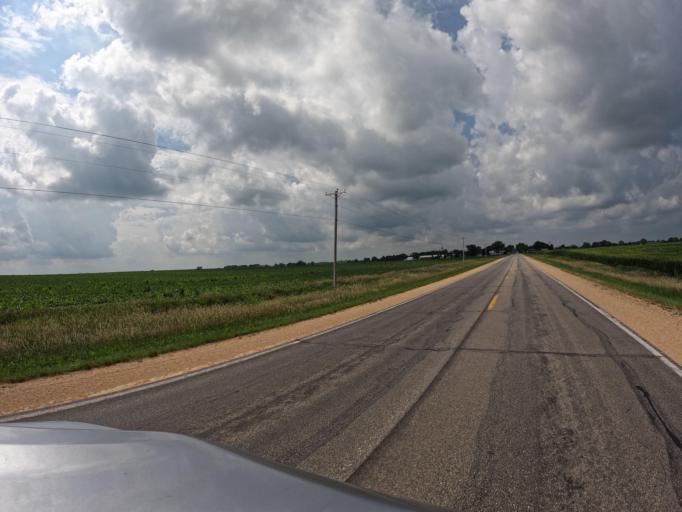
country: US
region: Iowa
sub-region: Clinton County
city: Camanche
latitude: 41.7935
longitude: -90.3549
